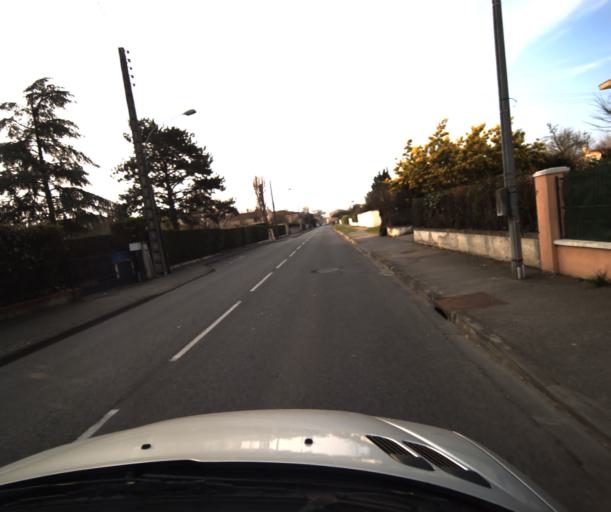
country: FR
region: Midi-Pyrenees
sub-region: Departement de la Haute-Garonne
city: Castelginest
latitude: 43.6896
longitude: 1.4340
